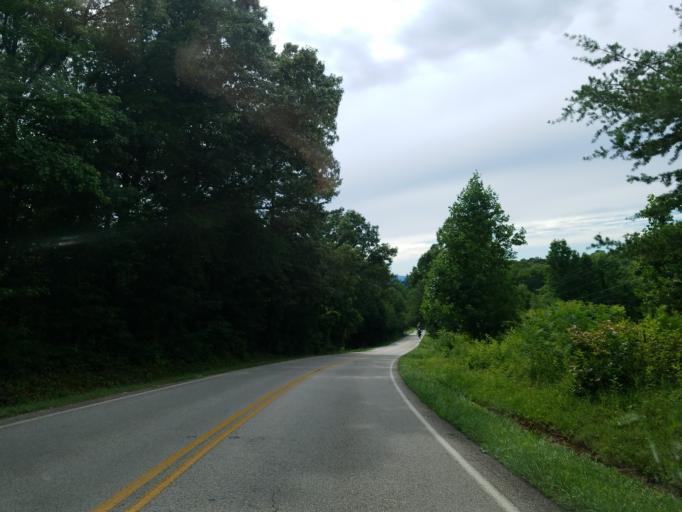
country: US
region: Georgia
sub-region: Lumpkin County
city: Dahlonega
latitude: 34.5577
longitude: -83.9145
